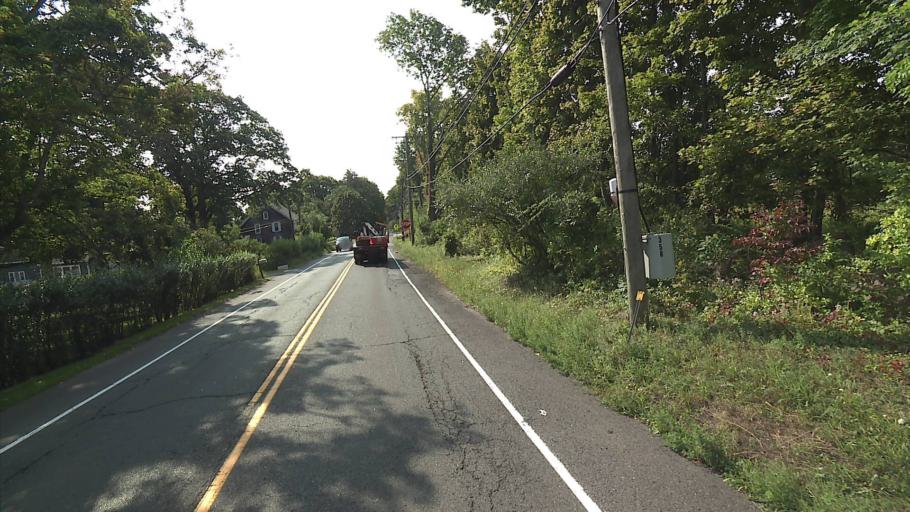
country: US
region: Connecticut
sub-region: Fairfield County
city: Bethel
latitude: 41.3148
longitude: -73.3511
